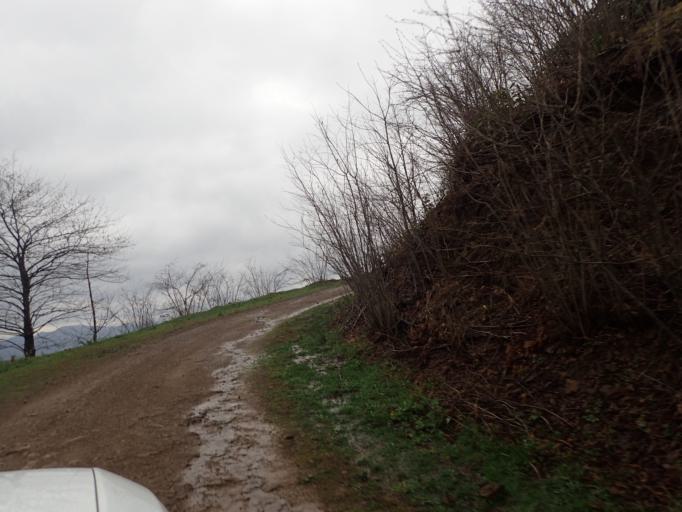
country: TR
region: Ordu
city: Camas
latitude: 40.8586
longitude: 37.5093
